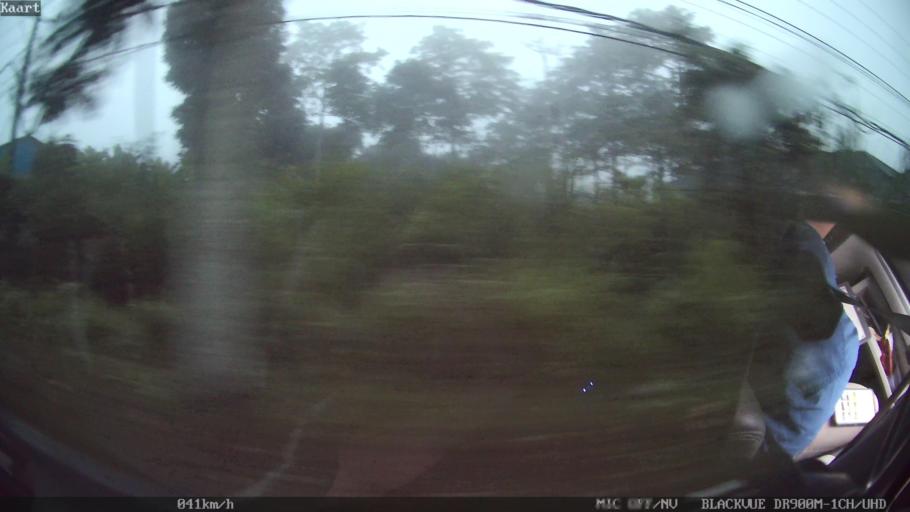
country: ID
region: Bali
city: Banjar Taro Kelod
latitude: -8.3186
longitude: 115.2985
